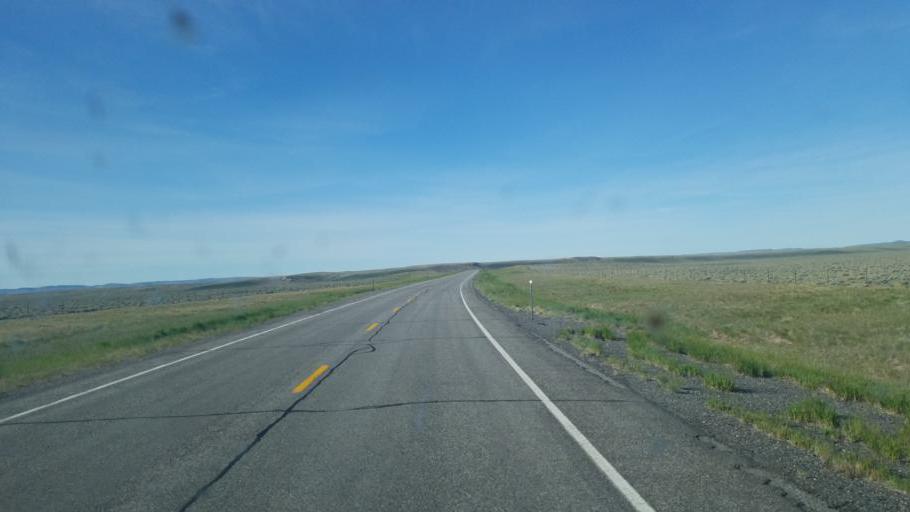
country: US
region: Wyoming
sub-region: Fremont County
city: Riverton
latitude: 42.6353
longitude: -108.1939
